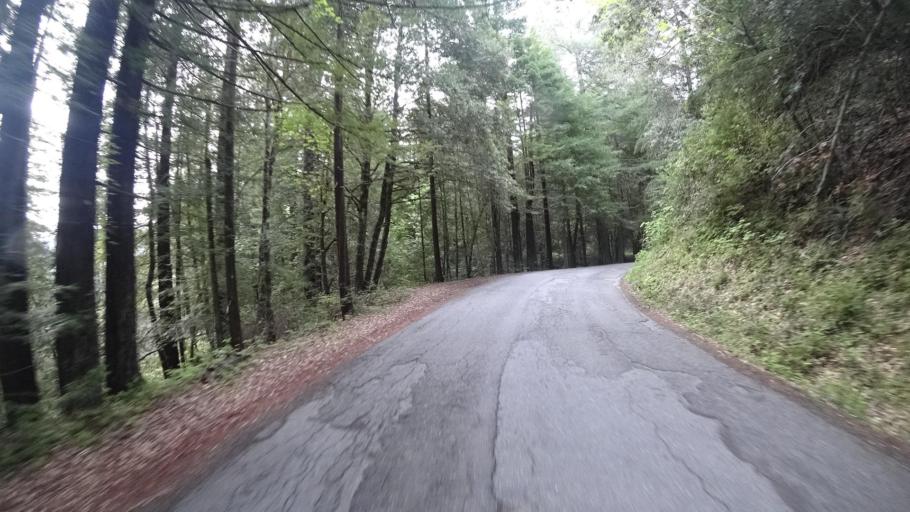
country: US
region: California
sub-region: Humboldt County
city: Redway
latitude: 40.3398
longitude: -123.9137
